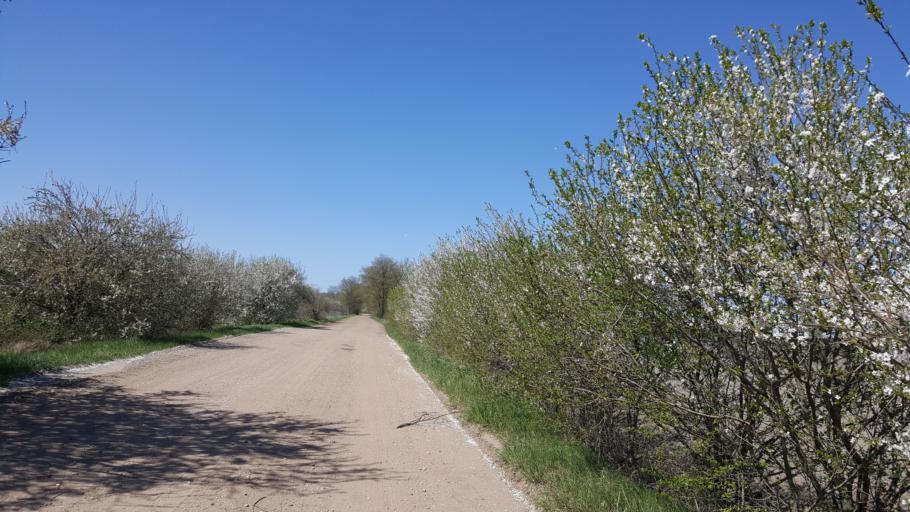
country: BY
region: Brest
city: Kamyanyets
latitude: 52.3284
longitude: 23.7630
